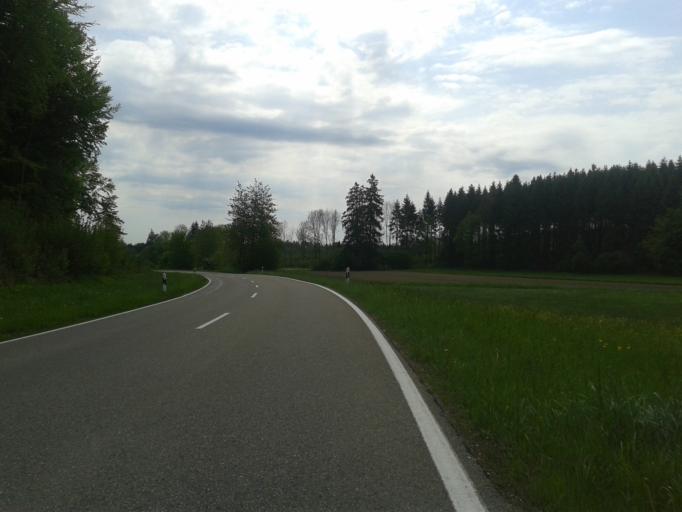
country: DE
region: Baden-Wuerttemberg
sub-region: Tuebingen Region
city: Erbach
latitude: 48.3545
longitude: 9.8469
